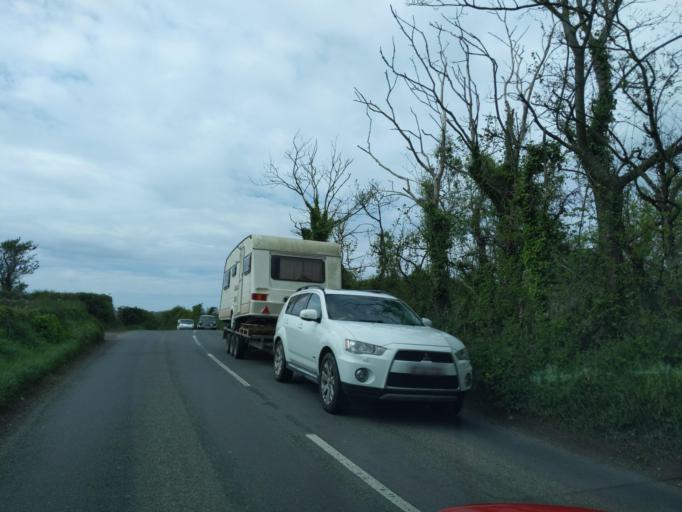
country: GB
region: England
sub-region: Cornwall
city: Wadebridge
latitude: 50.5359
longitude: -4.8493
